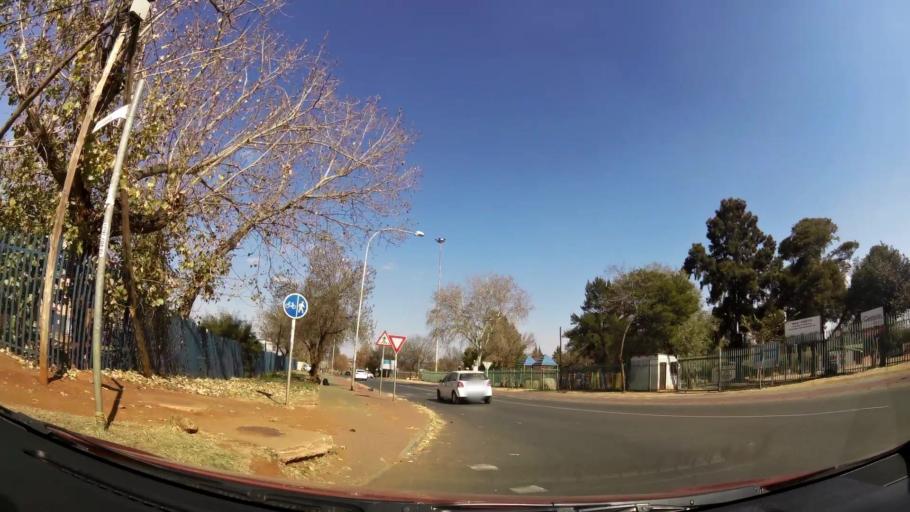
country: ZA
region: Gauteng
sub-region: City of Johannesburg Metropolitan Municipality
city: Soweto
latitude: -26.2456
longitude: 27.8937
